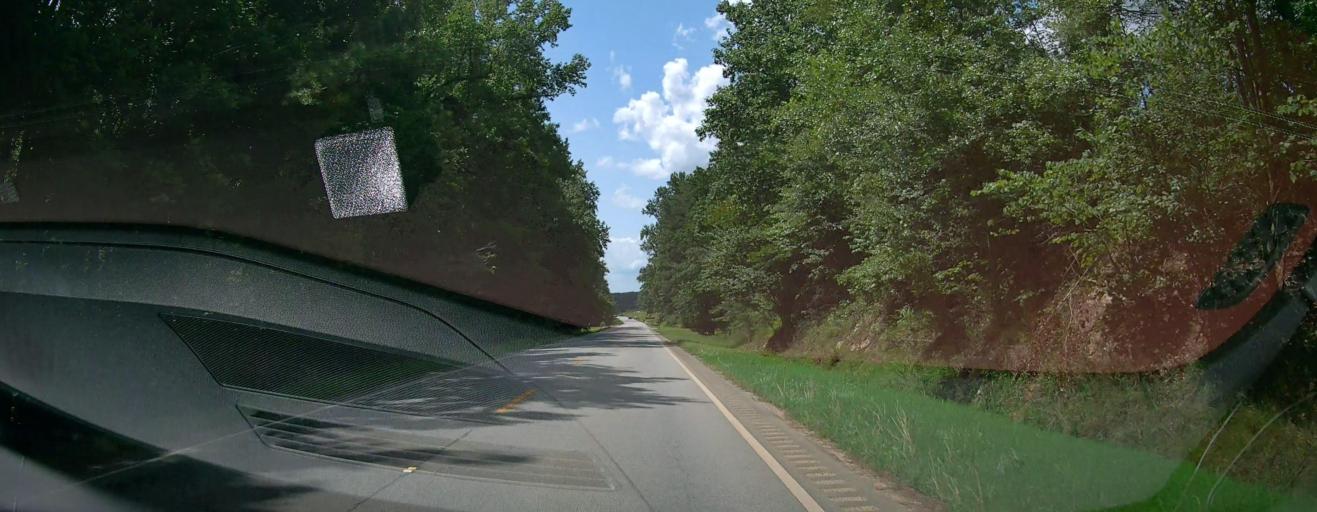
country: US
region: Alabama
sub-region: Cleburne County
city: Heflin
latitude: 33.5681
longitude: -85.4408
